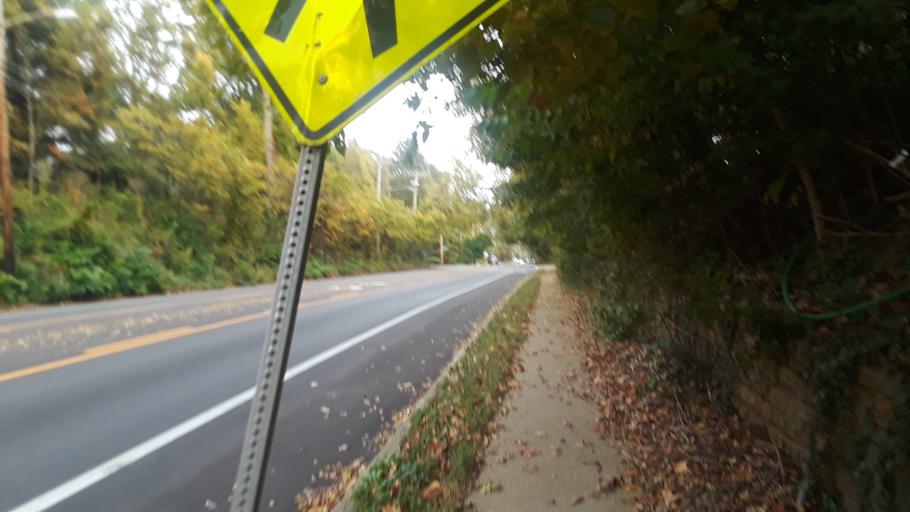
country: US
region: Kentucky
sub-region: Jefferson County
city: Saint Matthews
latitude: 38.2451
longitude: -85.6947
